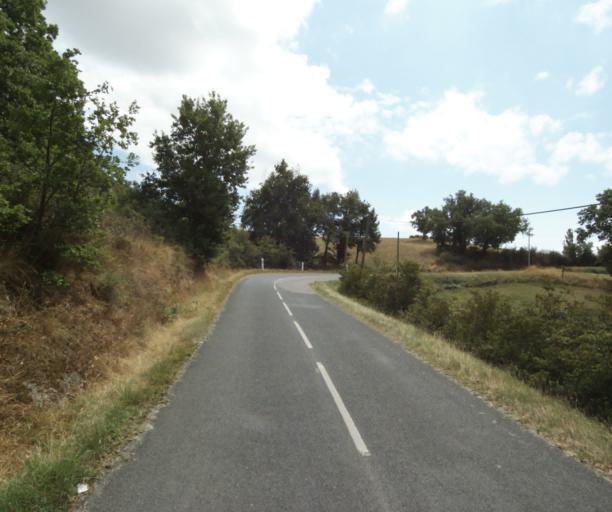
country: FR
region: Midi-Pyrenees
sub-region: Departement de la Haute-Garonne
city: Revel
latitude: 43.4431
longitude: 1.9877
